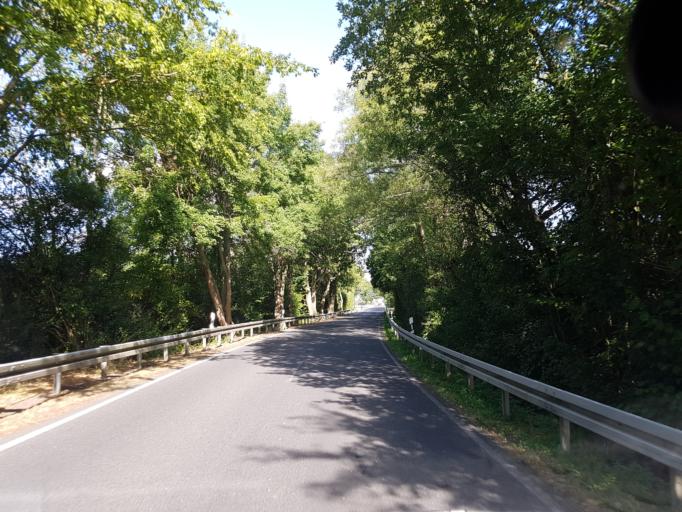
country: DE
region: Brandenburg
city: Sonnewalde
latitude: 51.7022
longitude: 13.6452
